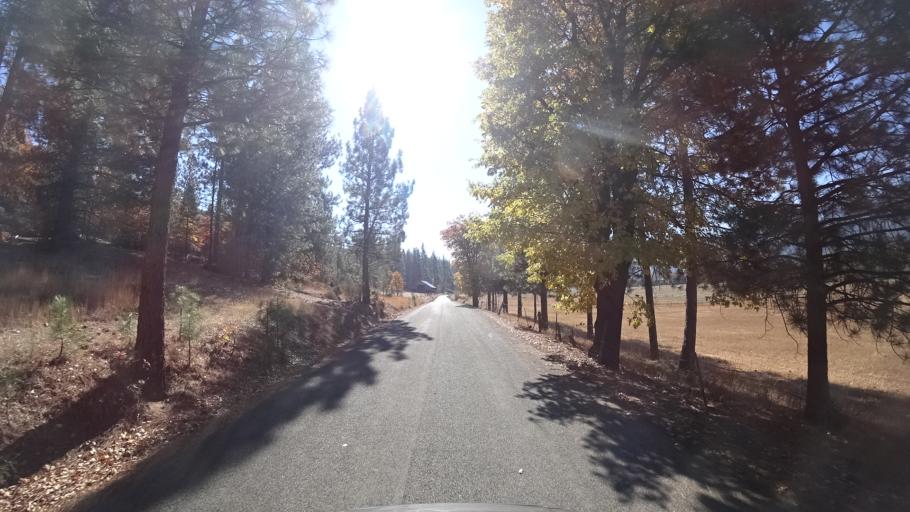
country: US
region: California
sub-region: Siskiyou County
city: Yreka
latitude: 41.5892
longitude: -122.9564
